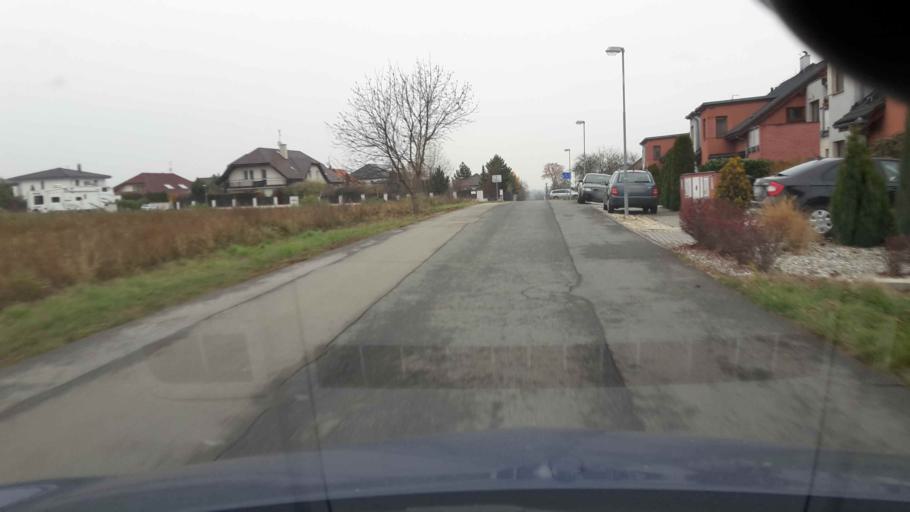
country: CZ
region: Olomoucky
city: Horka nad Moravou
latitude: 49.6101
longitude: 17.2069
